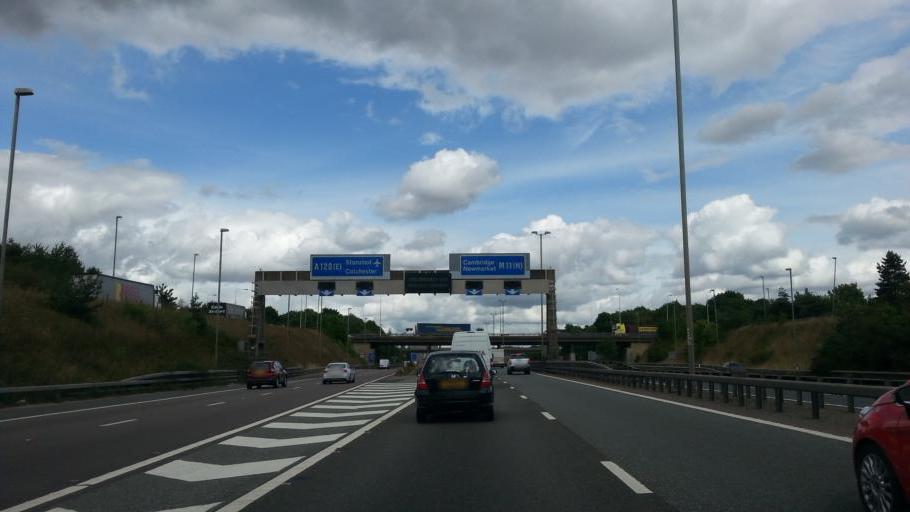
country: GB
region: England
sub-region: Essex
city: Stansted
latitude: 51.8694
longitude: 0.1976
